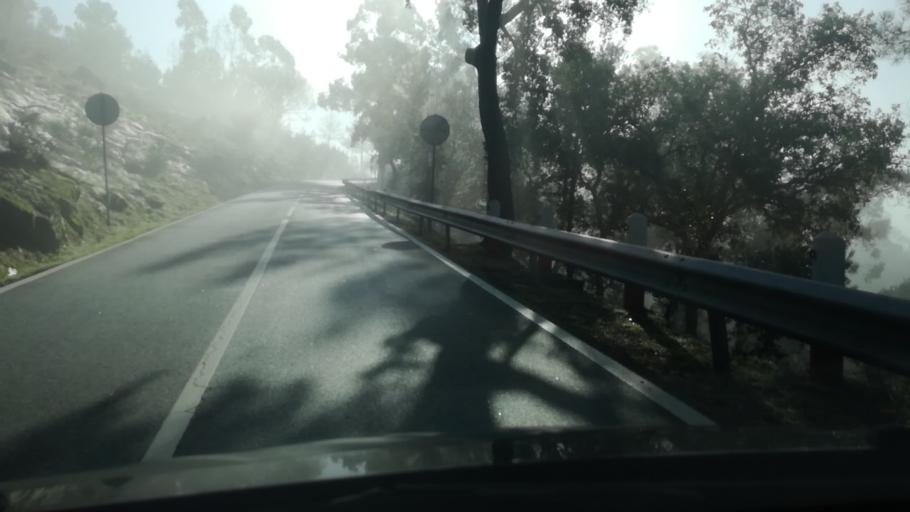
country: PT
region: Braga
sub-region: Guimaraes
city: Ponte
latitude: 41.5281
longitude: -8.3194
